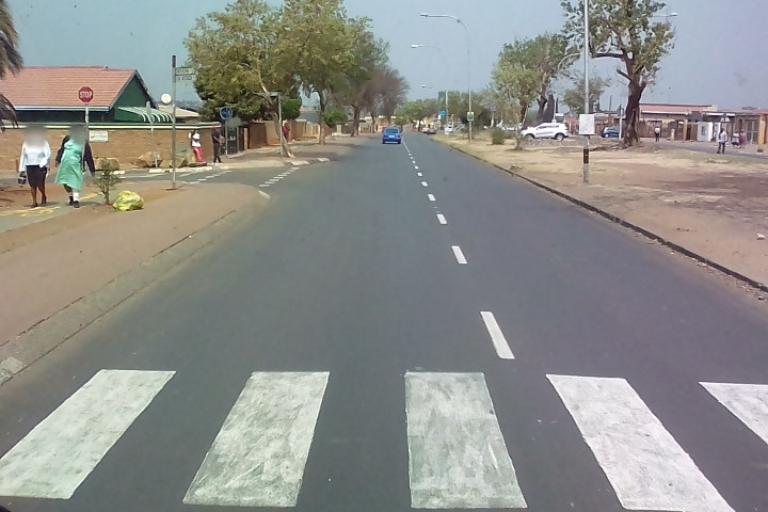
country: ZA
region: Gauteng
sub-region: City of Johannesburg Metropolitan Municipality
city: Soweto
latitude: -26.2479
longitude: 27.8834
